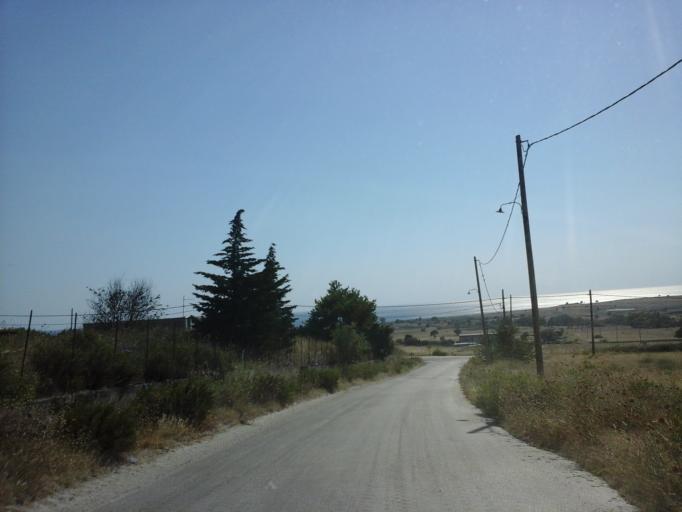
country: GR
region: East Macedonia and Thrace
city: Kamariotissa
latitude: 40.4605
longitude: 25.4972
